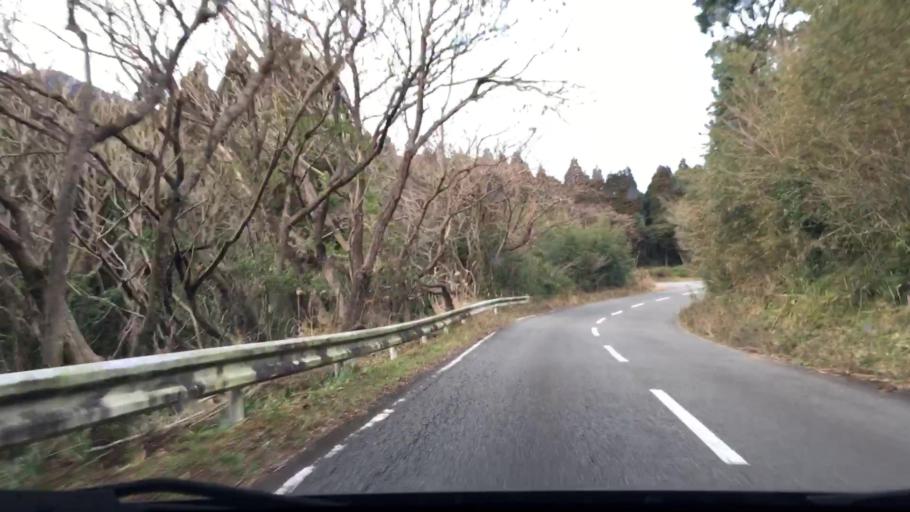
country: JP
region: Miyazaki
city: Nichinan
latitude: 31.6622
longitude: 131.3167
